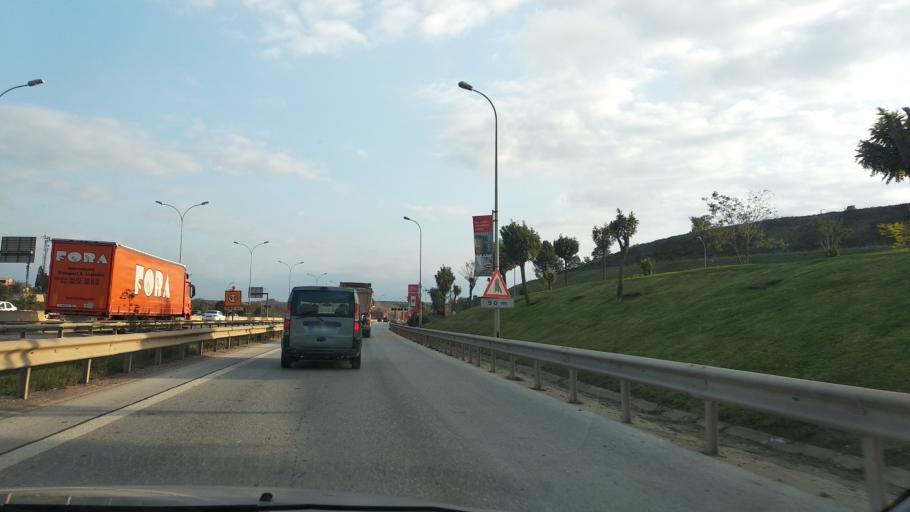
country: TR
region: Istanbul
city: Pendik
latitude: 40.9134
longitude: 29.3251
